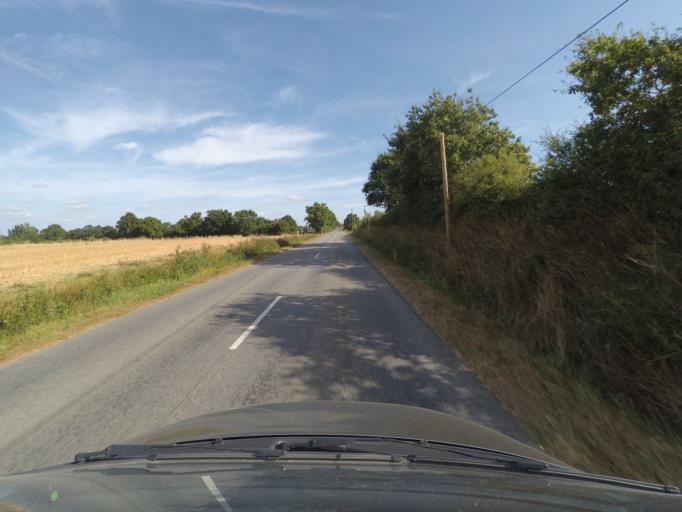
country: FR
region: Pays de la Loire
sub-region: Departement de la Loire-Atlantique
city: Vieillevigne
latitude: 46.9881
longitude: -1.4463
